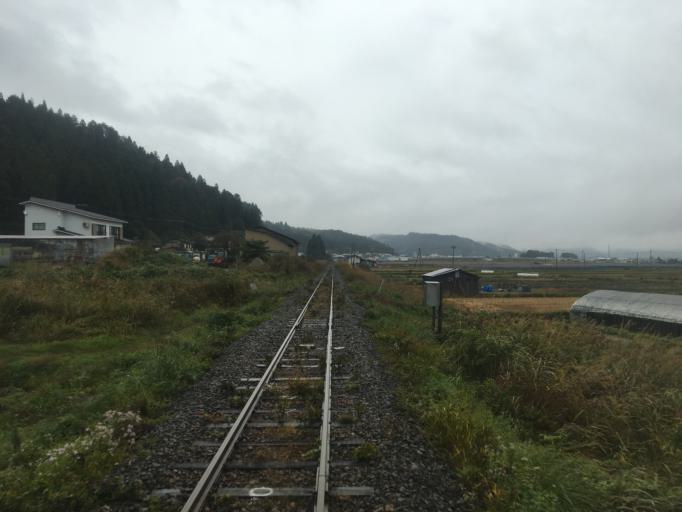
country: JP
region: Yamagata
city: Obanazawa
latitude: 38.7647
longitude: 140.5014
